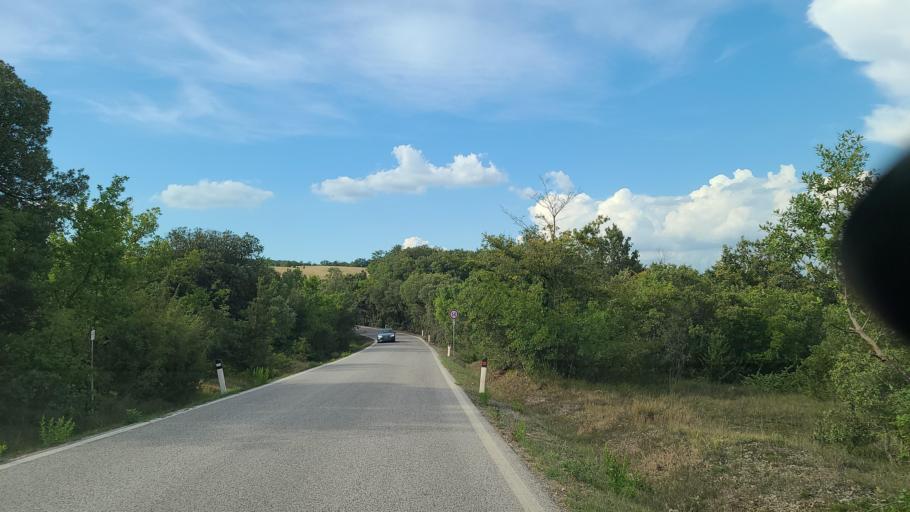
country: IT
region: Tuscany
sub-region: Provincia di Siena
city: San Gimignano
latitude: 43.4238
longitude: 10.9756
